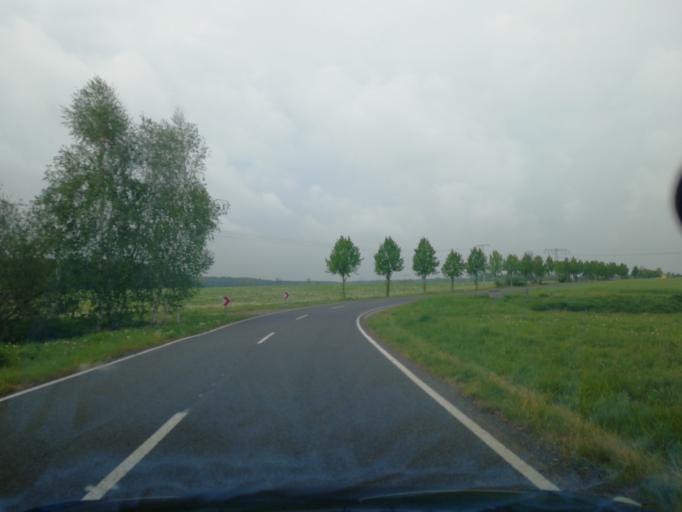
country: DE
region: Brandenburg
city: Calau
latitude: 51.7486
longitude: 13.9774
